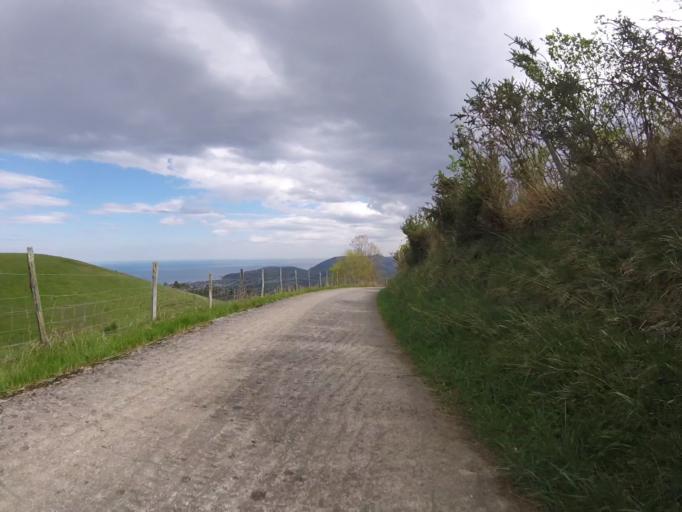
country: ES
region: Basque Country
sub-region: Provincia de Guipuzcoa
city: Zarautz
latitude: 43.2475
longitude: -2.1898
